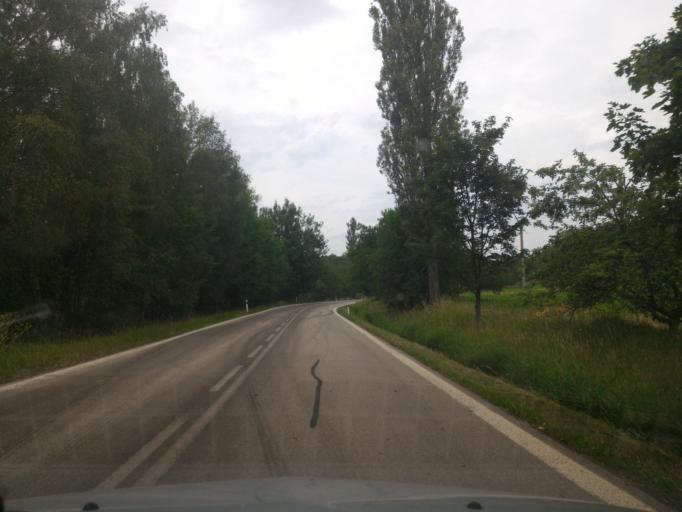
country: CZ
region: Jihocesky
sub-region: Okres Jindrichuv Hradec
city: Studena
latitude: 49.1888
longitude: 15.3658
